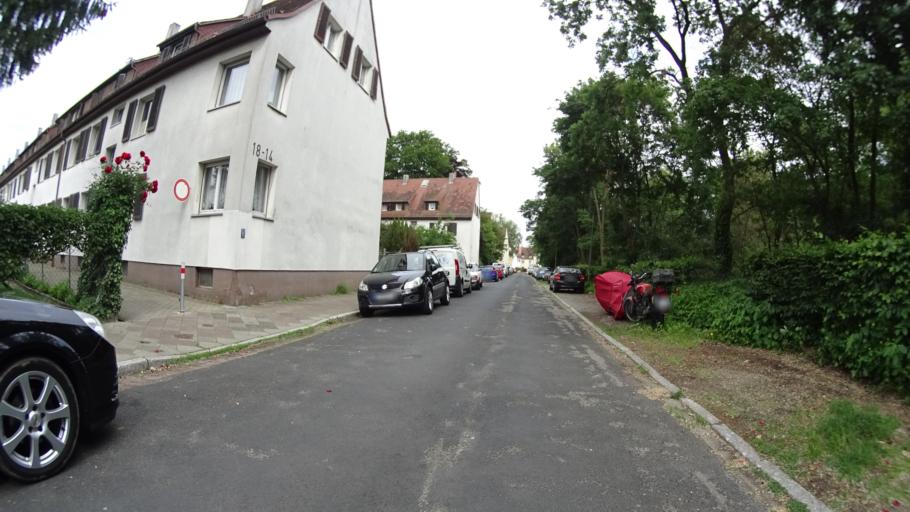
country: DE
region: Baden-Wuerttemberg
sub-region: Karlsruhe Region
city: Rheinstetten
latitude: 49.0063
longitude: 8.3397
